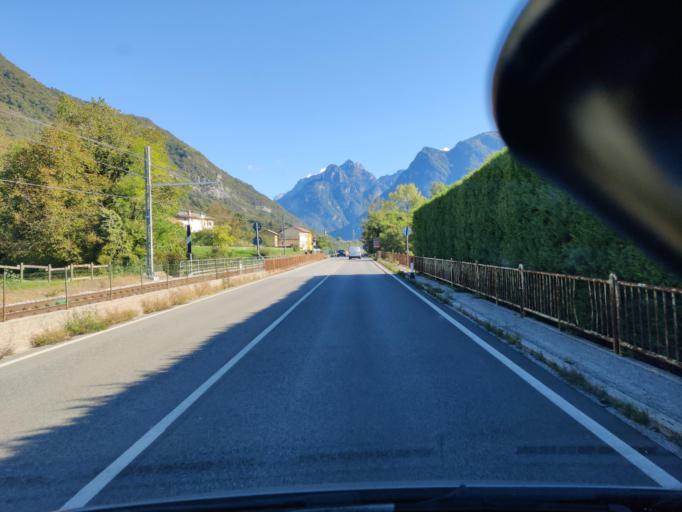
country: IT
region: Veneto
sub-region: Provincia di Belluno
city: Ponte nelle Alpi-Polpet
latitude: 46.1774
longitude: 12.2666
